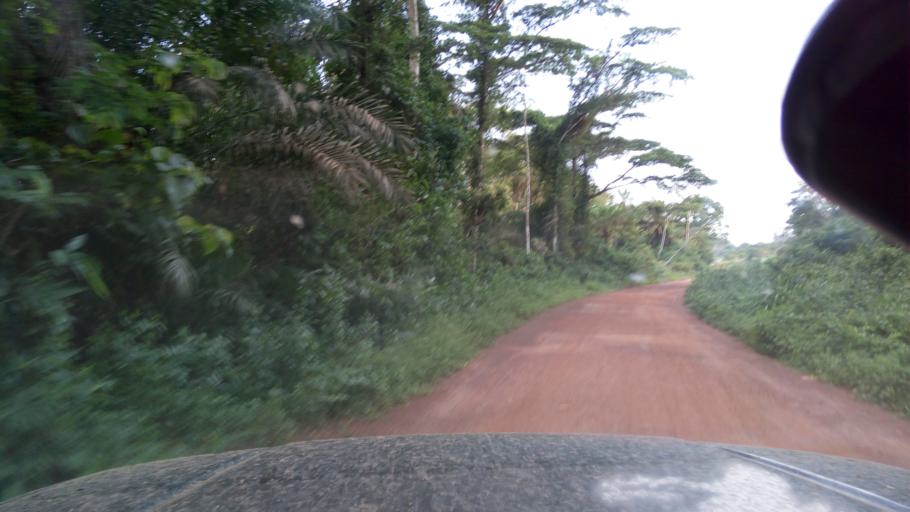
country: SL
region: Eastern Province
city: Gorahun
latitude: 7.5864
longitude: -11.1494
